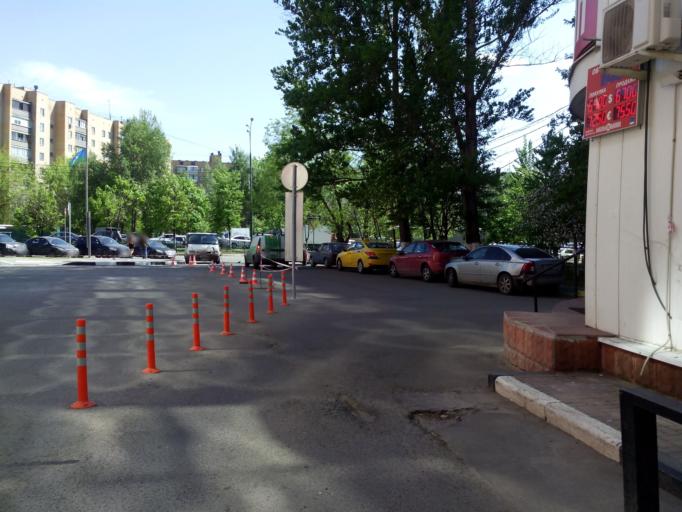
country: RU
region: Moskovskaya
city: Odintsovo
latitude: 55.6775
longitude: 37.2801
